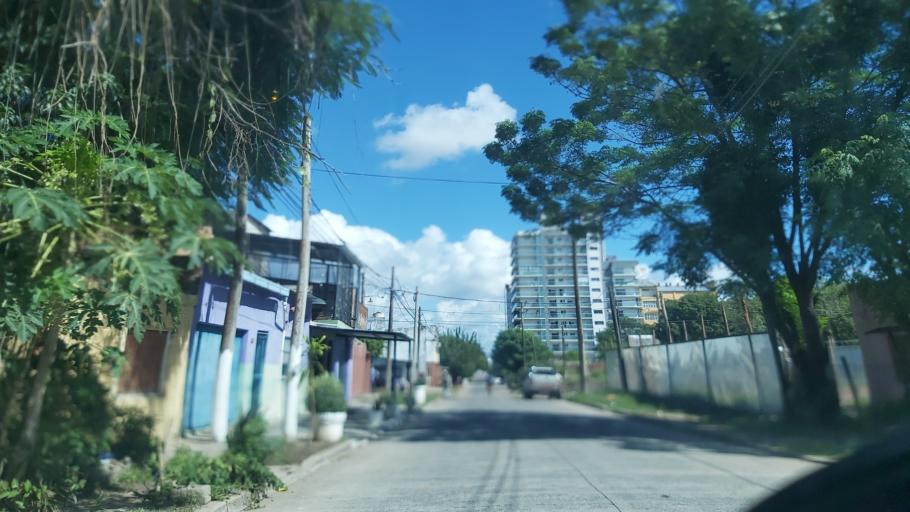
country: AR
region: Corrientes
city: Corrientes
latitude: -27.4765
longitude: -58.8506
